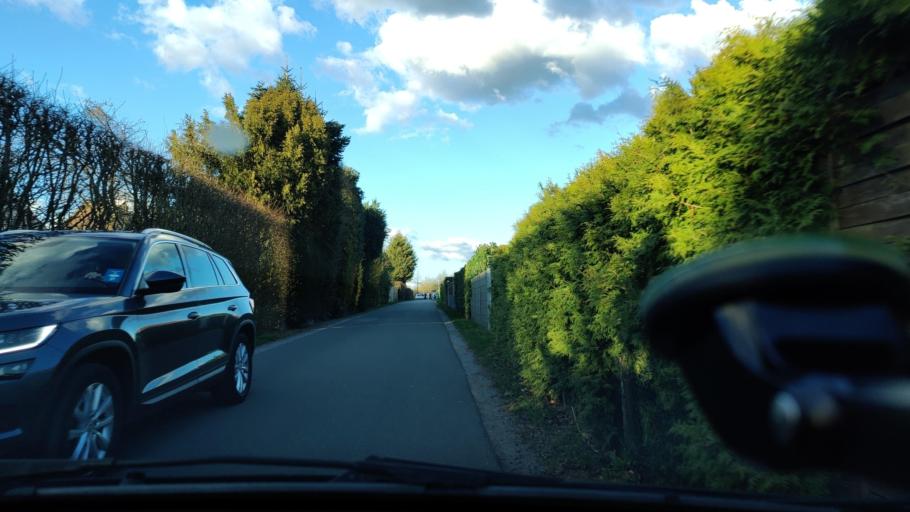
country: DE
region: North Rhine-Westphalia
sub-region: Regierungsbezirk Munster
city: Coesfeld
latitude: 51.8951
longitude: 7.1980
